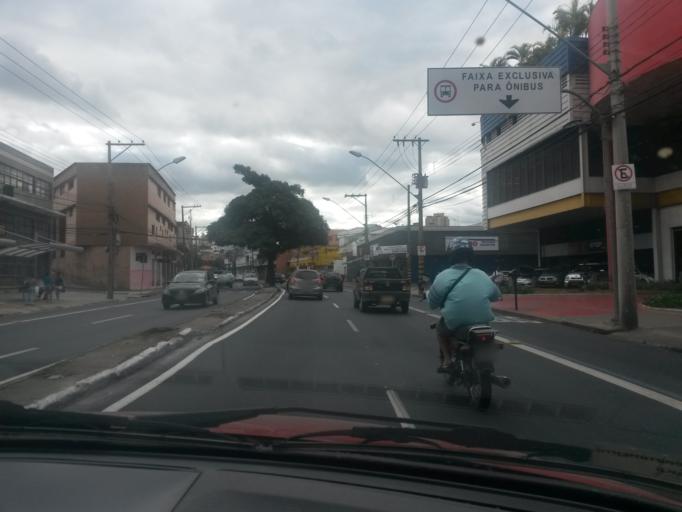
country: BR
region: Minas Gerais
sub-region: Belo Horizonte
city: Belo Horizonte
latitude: -19.9082
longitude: -43.9591
